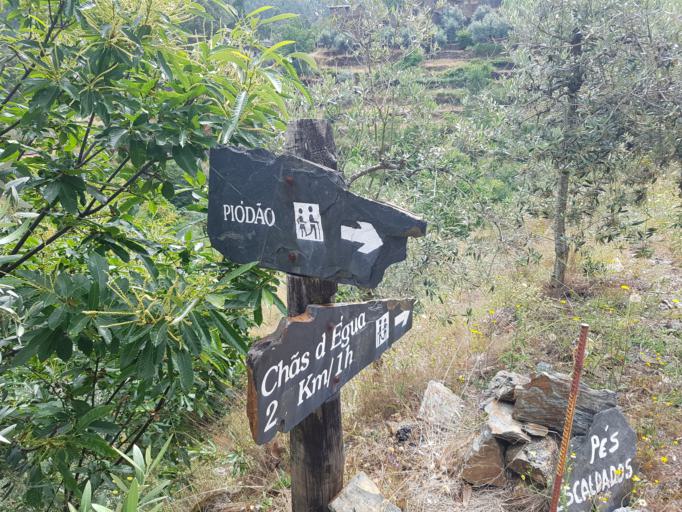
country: PT
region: Coimbra
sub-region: Oliveira do Hospital
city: Oliveira do Hospital
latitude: 40.2393
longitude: -7.8064
